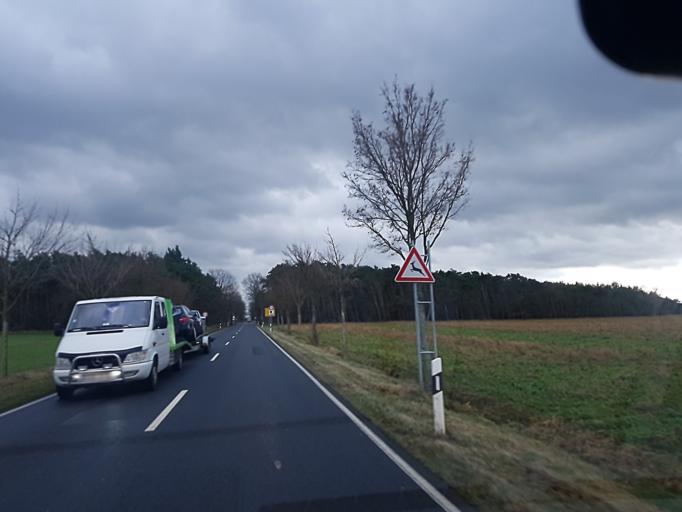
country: DE
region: Brandenburg
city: Bad Liebenwerda
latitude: 51.4913
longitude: 13.3901
